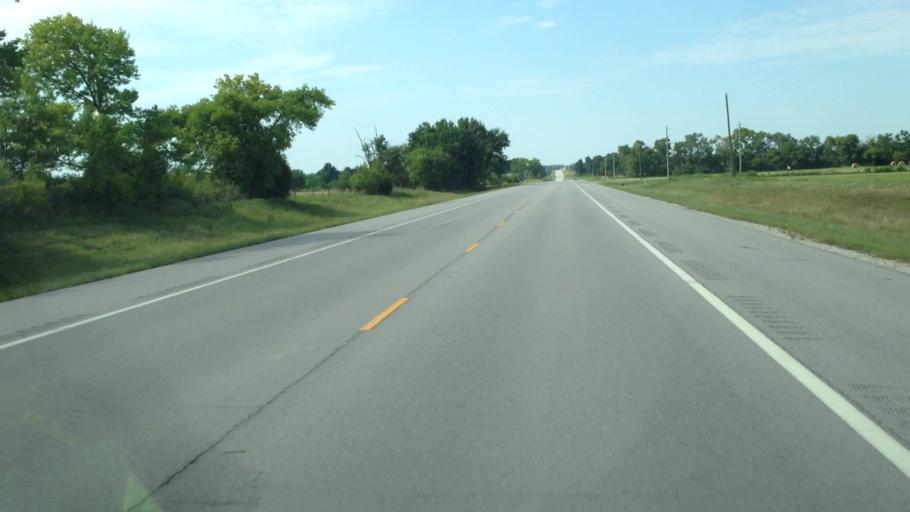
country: US
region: Kansas
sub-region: Labette County
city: Altamont
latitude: 37.2595
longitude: -95.2672
